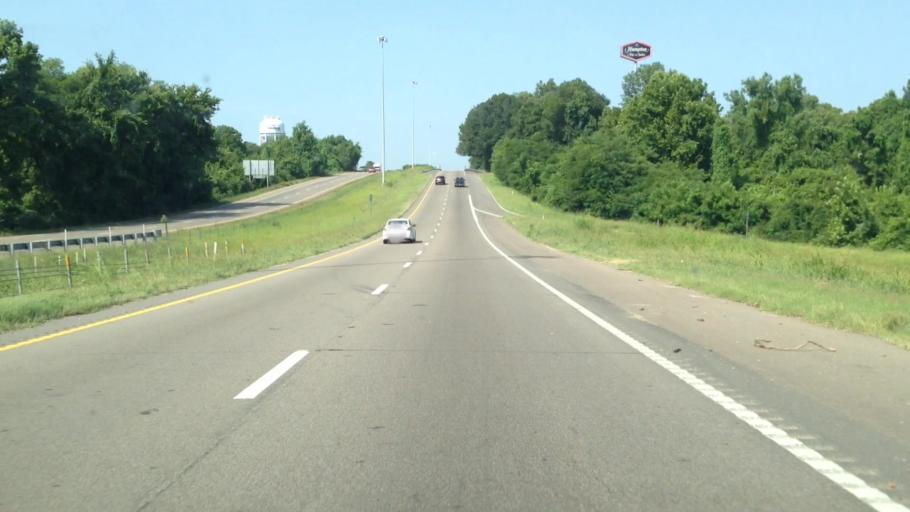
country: US
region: Mississippi
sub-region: Warren County
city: Beechwood
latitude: 32.3424
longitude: -90.8447
